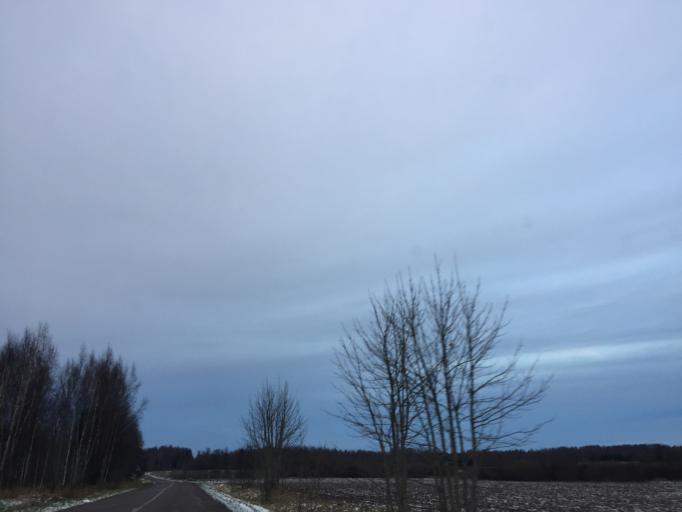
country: LV
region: Aloja
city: Aloja
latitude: 57.6242
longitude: 24.9322
